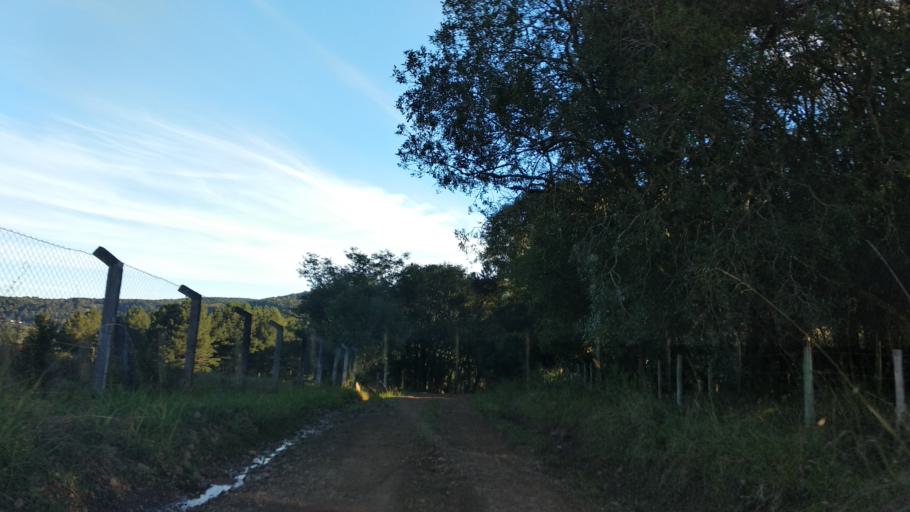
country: BR
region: Santa Catarina
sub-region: Celso Ramos
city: Celso Ramos
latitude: -27.5587
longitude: -51.2341
